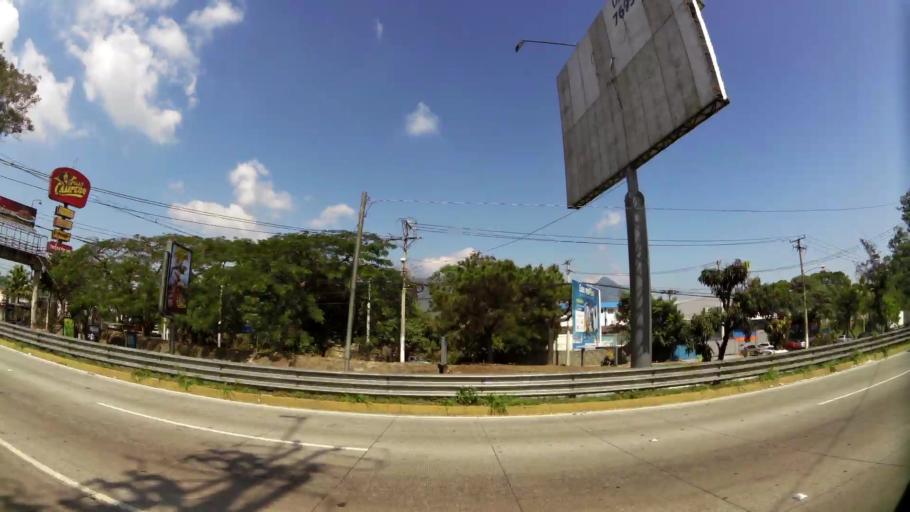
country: SV
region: La Libertad
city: Antiguo Cuscatlan
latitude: 13.6708
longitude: -89.2625
